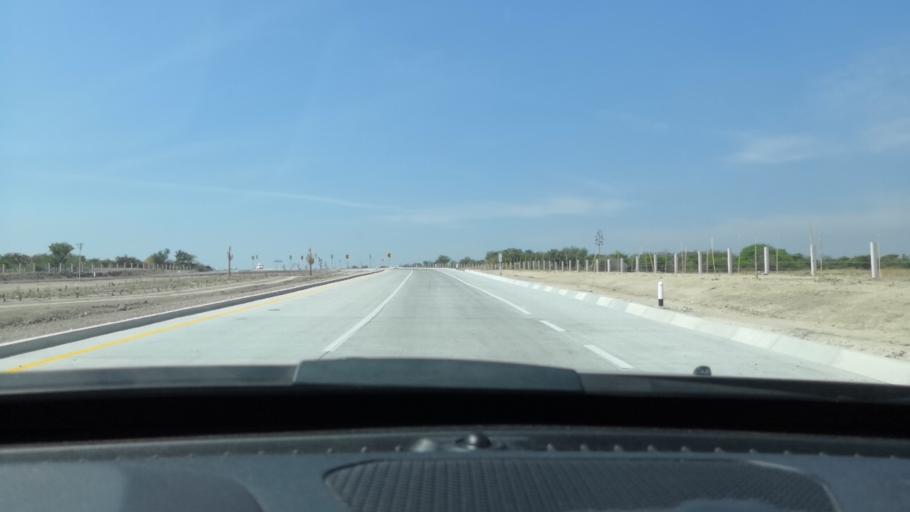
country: MX
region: Guanajuato
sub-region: Leon
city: Centro Familiar la Soledad
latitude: 21.0952
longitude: -101.7873
